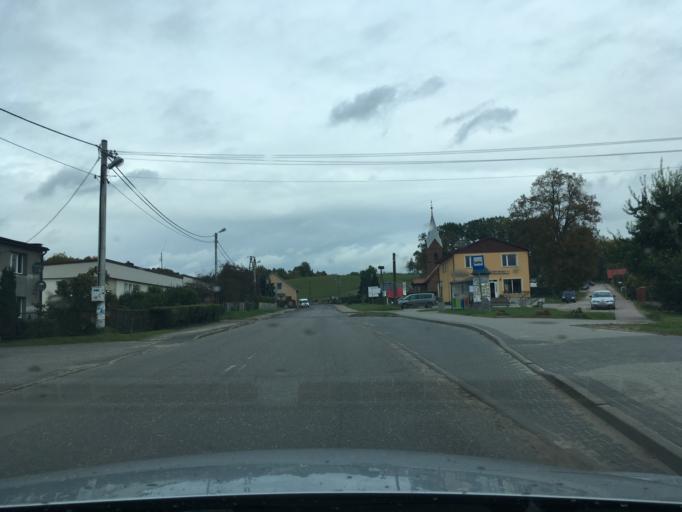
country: PL
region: Pomeranian Voivodeship
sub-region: Powiat gdanski
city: Przywidz
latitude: 54.1983
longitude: 18.3276
